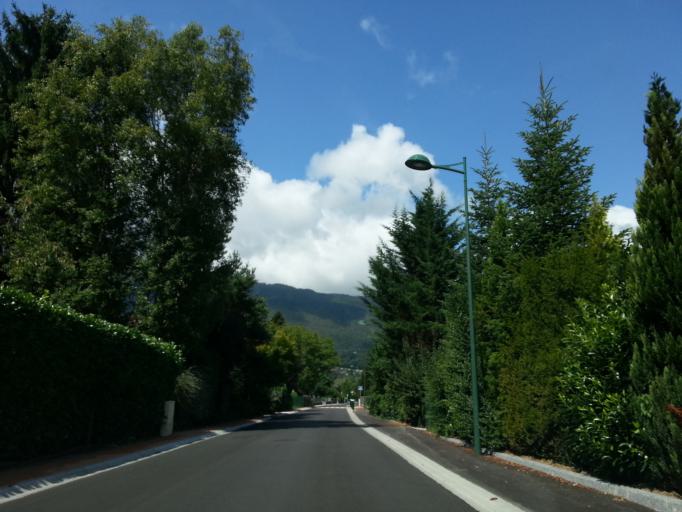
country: FR
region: Rhone-Alpes
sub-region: Departement de la Haute-Savoie
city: Saint-Jorioz
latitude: 45.8277
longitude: 6.1663
